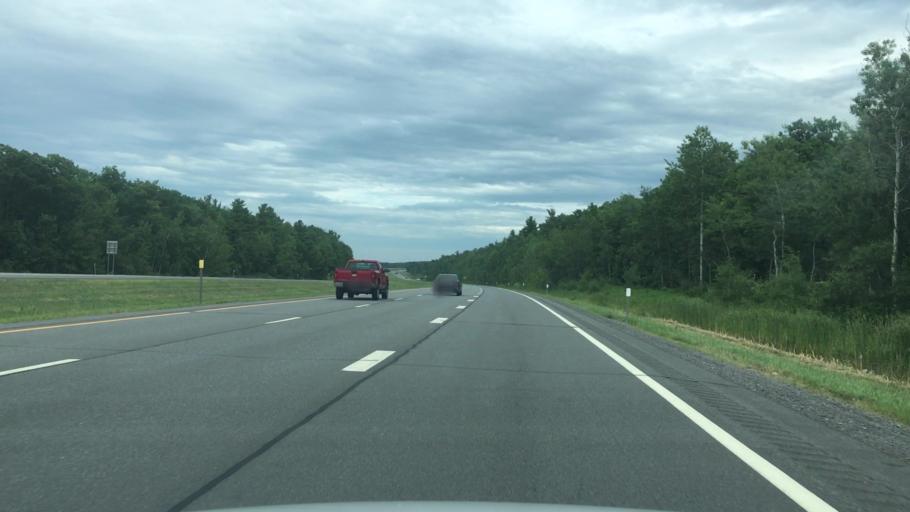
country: US
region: New York
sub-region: Schoharie County
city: Schoharie
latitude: 42.7165
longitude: -74.2600
